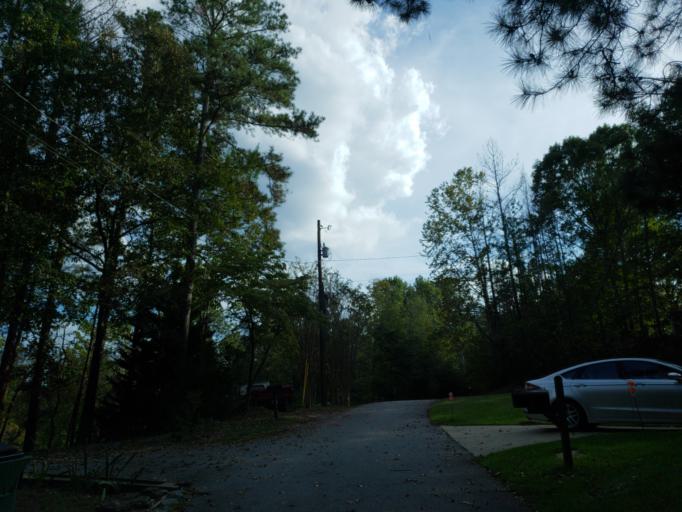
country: US
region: Georgia
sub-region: Fulton County
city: Roswell
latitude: 34.0875
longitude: -84.4212
